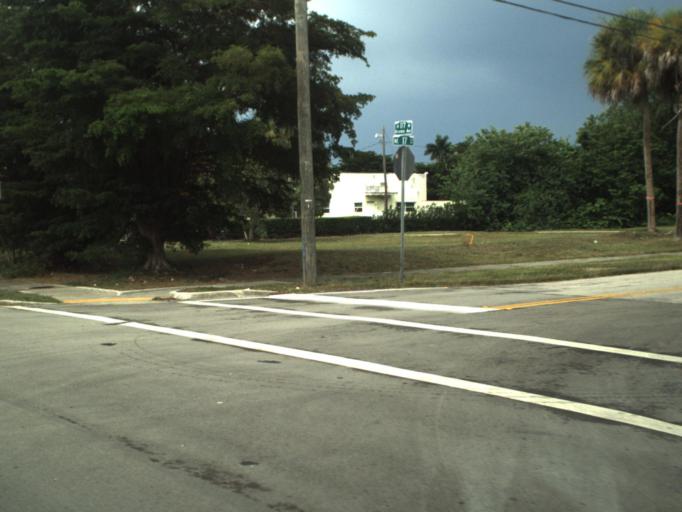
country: US
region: Florida
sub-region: Miami-Dade County
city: Homestead
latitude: 25.4862
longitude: -80.4775
